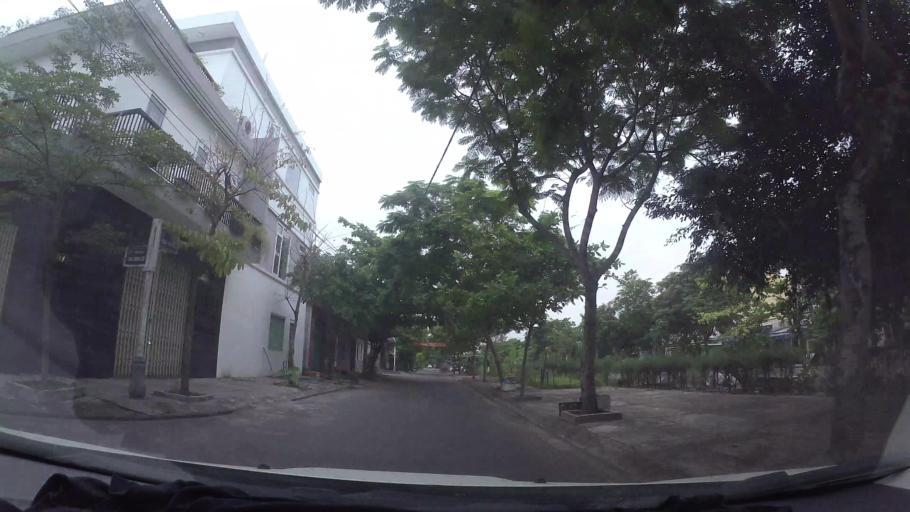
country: VN
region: Da Nang
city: Lien Chieu
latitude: 16.0789
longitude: 108.1604
